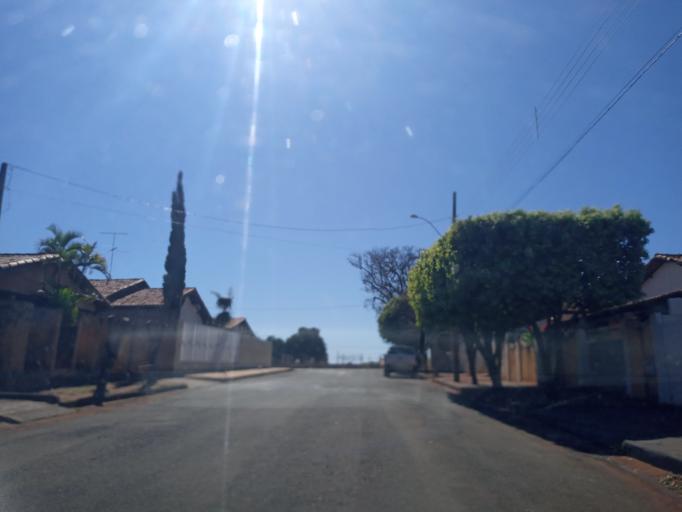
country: BR
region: Minas Gerais
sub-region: Ituiutaba
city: Ituiutaba
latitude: -18.9624
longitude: -49.4558
